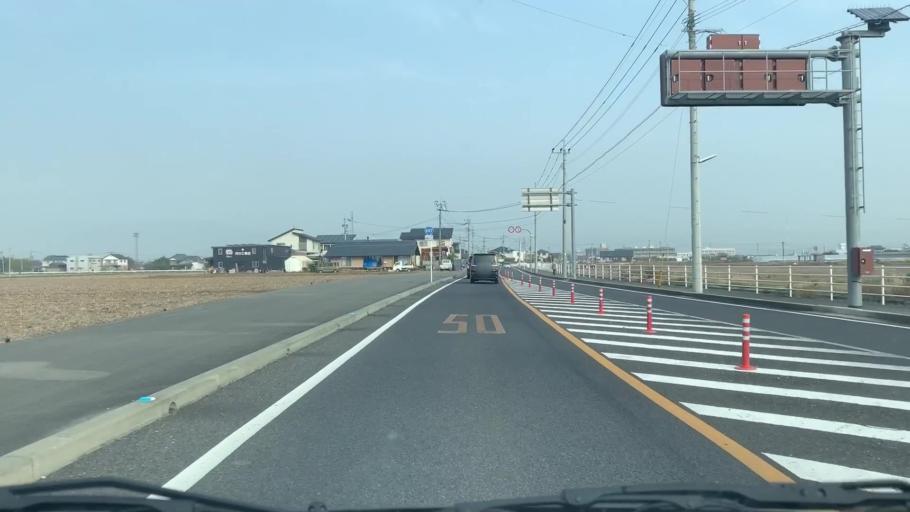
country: JP
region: Saga Prefecture
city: Saga-shi
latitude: 33.2325
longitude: 130.2576
